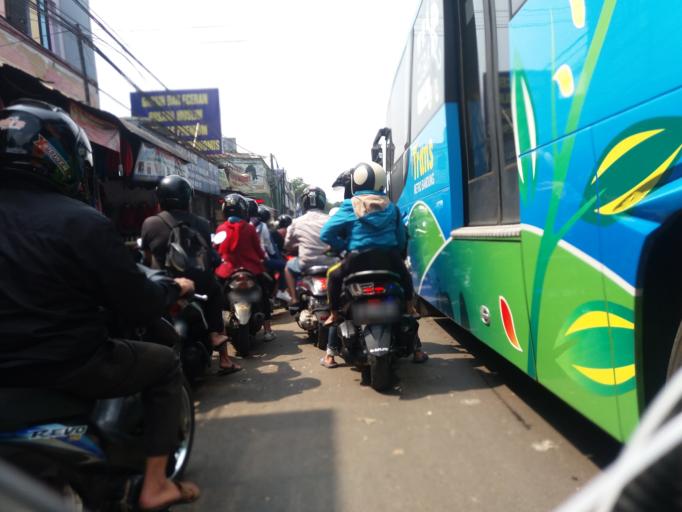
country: ID
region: West Java
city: Bandung
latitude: -6.9163
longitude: 107.5893
